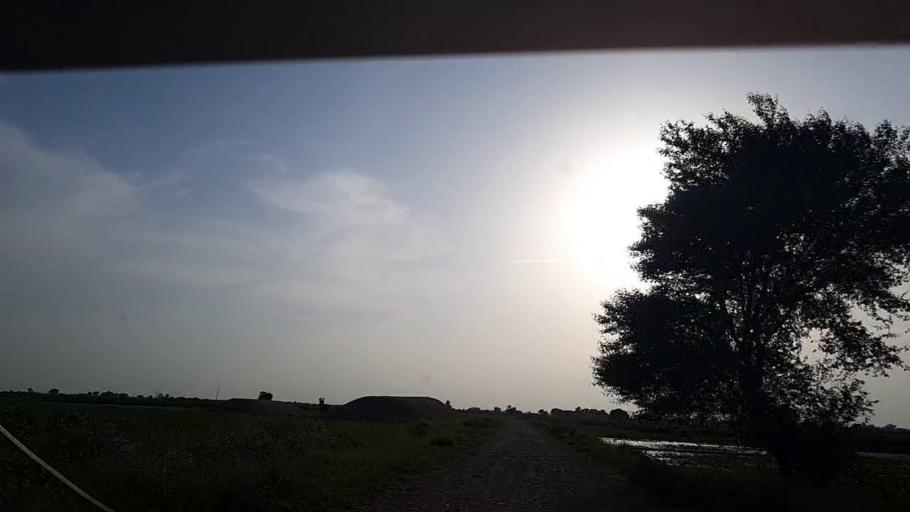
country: PK
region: Sindh
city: Khanpur
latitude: 27.8088
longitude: 69.3228
